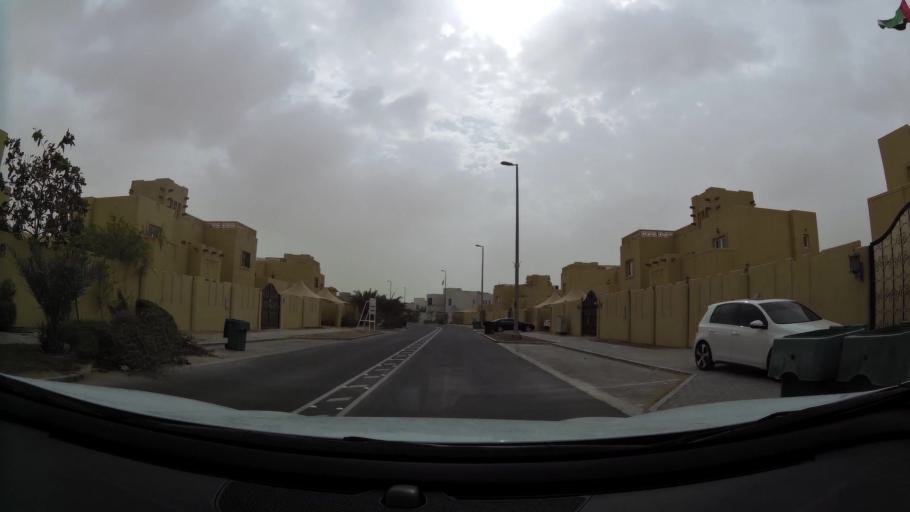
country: AE
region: Abu Dhabi
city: Abu Dhabi
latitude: 24.4538
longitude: 54.7203
